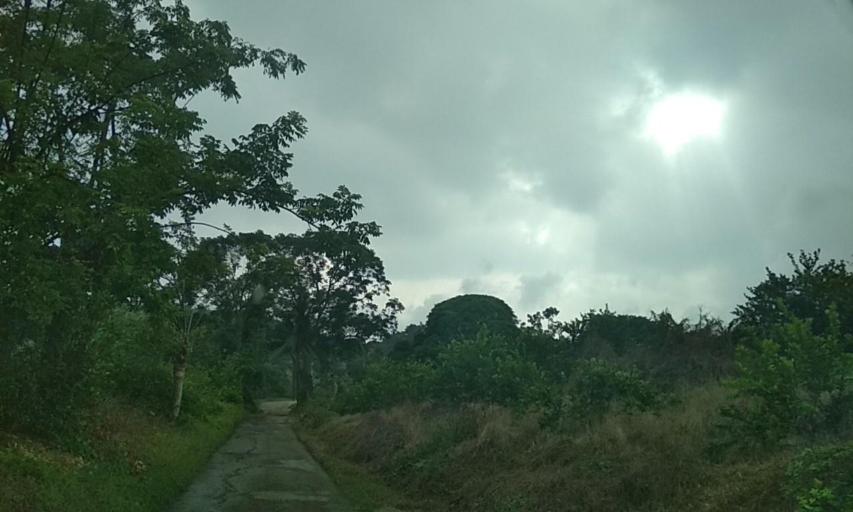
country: MX
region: Puebla
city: San Jose Acateno
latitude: 20.2276
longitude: -97.1201
